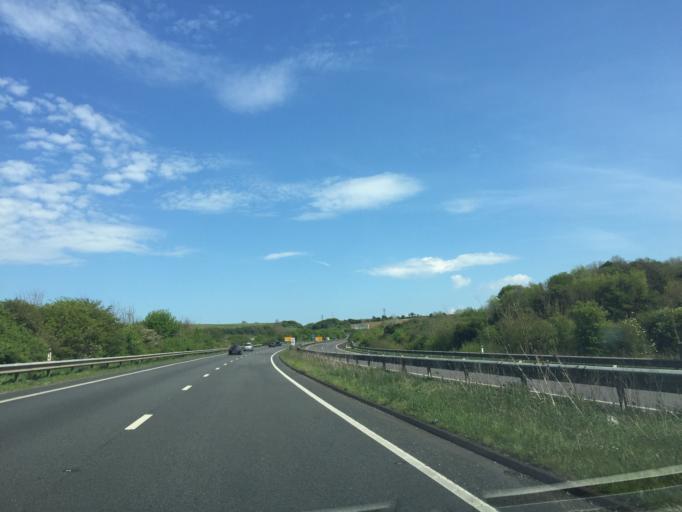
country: GB
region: England
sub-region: Kent
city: Hawkinge
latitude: 51.1124
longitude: 1.1901
